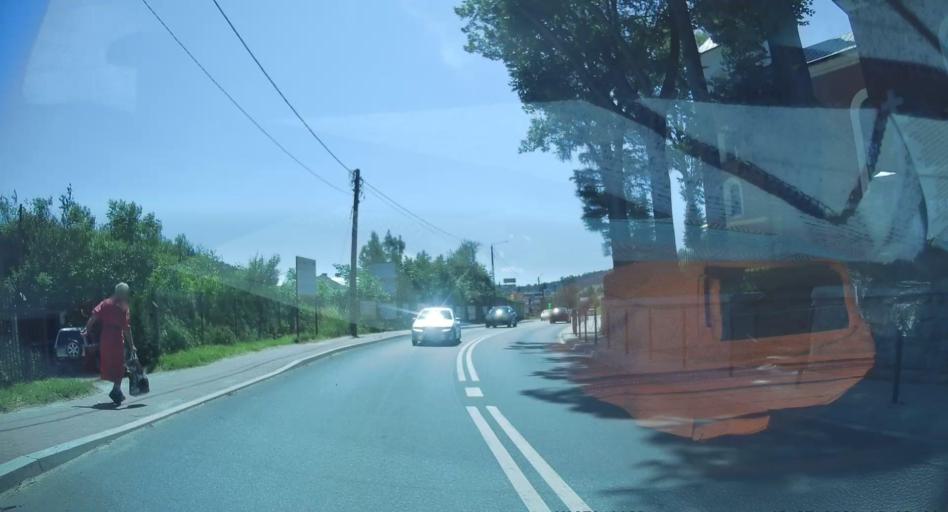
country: PL
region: Lesser Poland Voivodeship
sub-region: Powiat nowosadecki
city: Krynica-Zdroj
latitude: 49.3955
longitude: 20.9573
